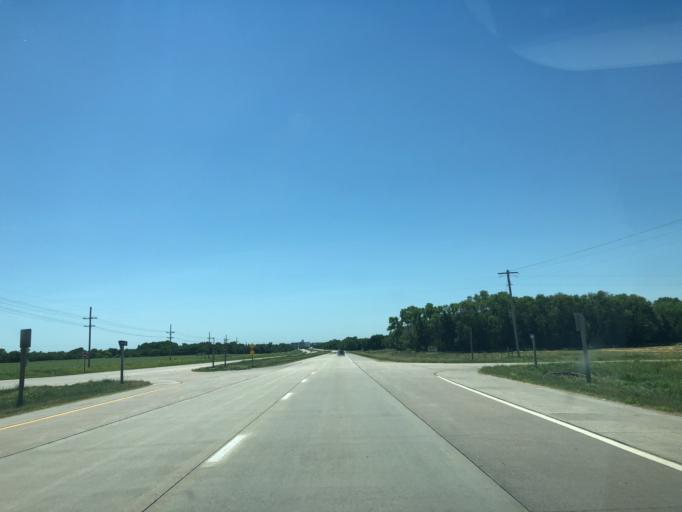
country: US
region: Kansas
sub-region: Cloud County
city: Concordia
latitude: 39.6034
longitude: -97.6601
